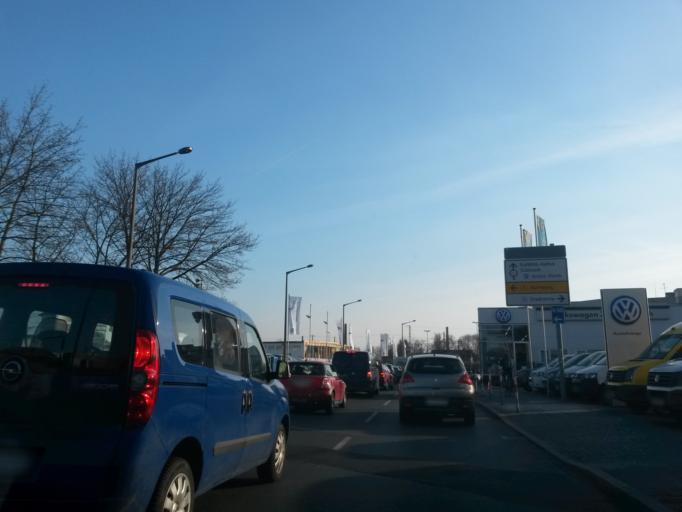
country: DE
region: Bavaria
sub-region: Regierungsbezirk Mittelfranken
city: Furth
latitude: 49.4667
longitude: 11.0130
